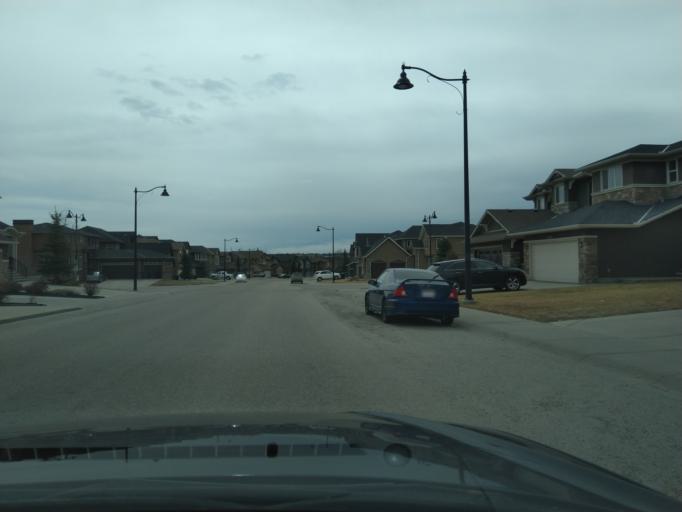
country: CA
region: Alberta
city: Calgary
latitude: 51.1680
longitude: -114.0809
